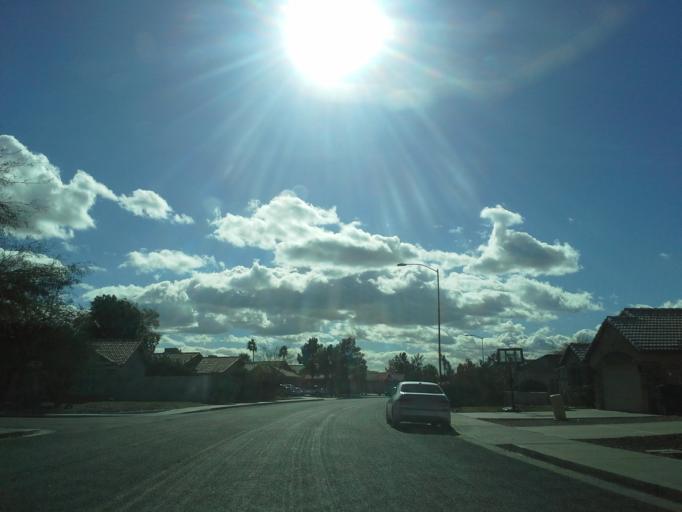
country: US
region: Arizona
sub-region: Maricopa County
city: Gilbert
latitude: 33.3993
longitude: -111.7142
